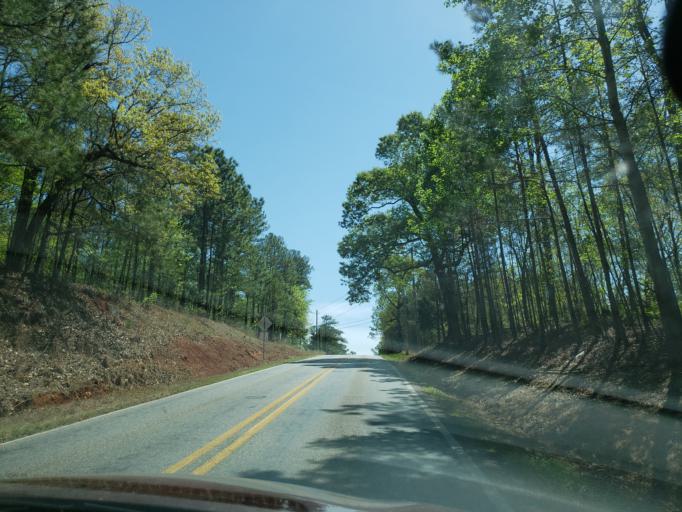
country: US
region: Alabama
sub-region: Tallapoosa County
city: Dadeville
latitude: 32.7070
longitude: -85.8217
